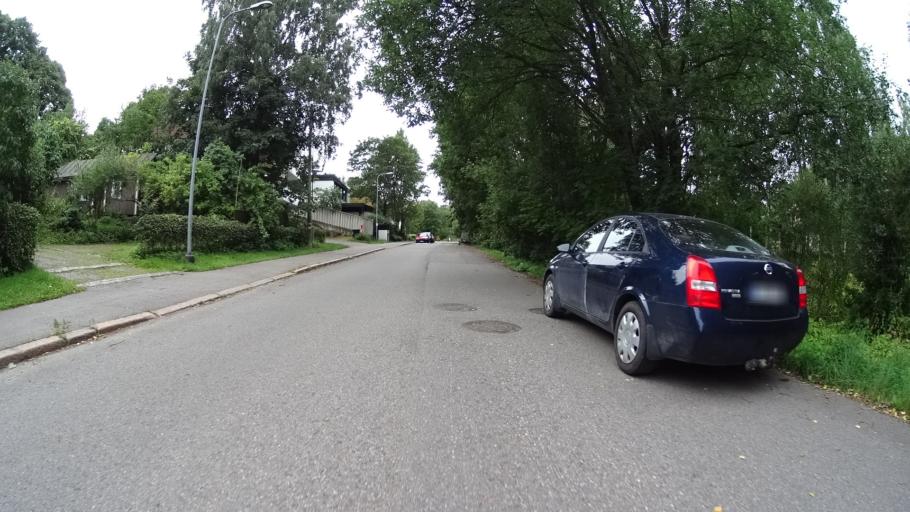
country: FI
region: Uusimaa
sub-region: Helsinki
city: Helsinki
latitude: 60.2251
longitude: 24.9390
